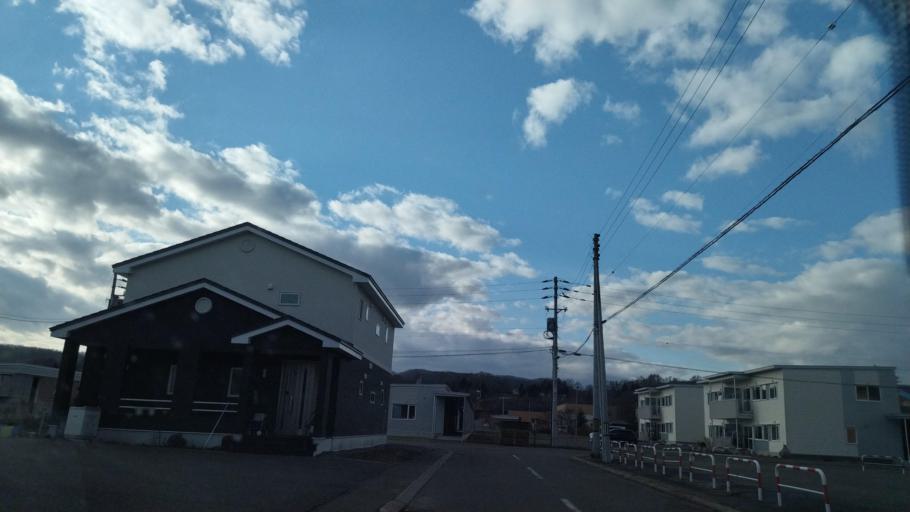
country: JP
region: Hokkaido
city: Otofuke
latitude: 43.2477
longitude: 143.5510
